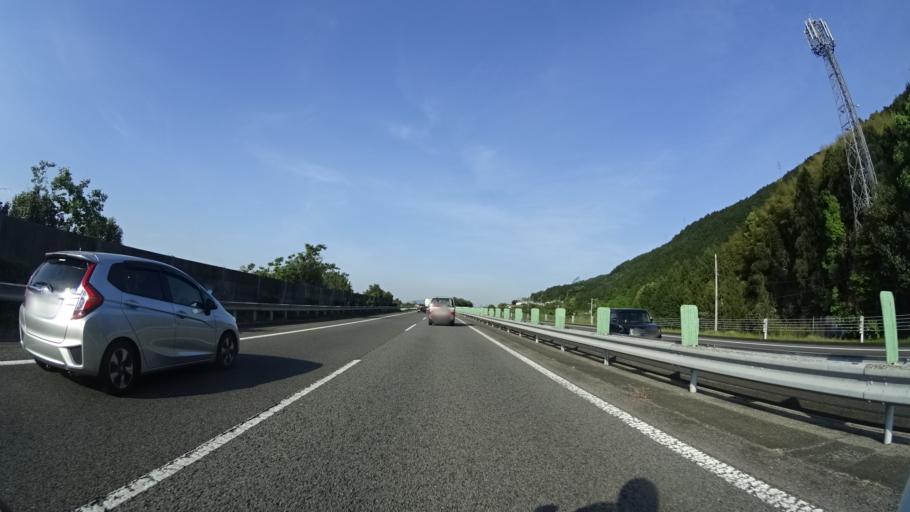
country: JP
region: Ehime
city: Kawanoecho
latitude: 33.9631
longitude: 133.5240
